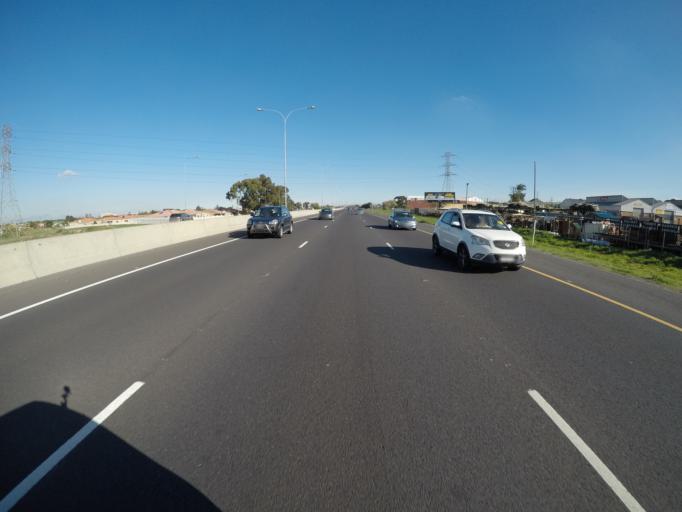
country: ZA
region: Western Cape
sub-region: City of Cape Town
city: Kraaifontein
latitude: -33.9093
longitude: 18.6713
